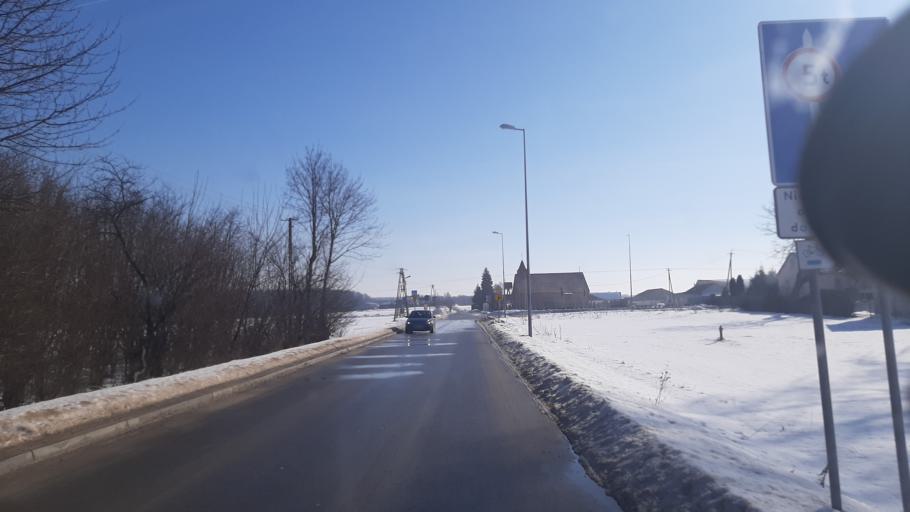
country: PL
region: Lublin Voivodeship
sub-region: Powiat lubelski
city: Garbow
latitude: 51.3050
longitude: 22.3070
